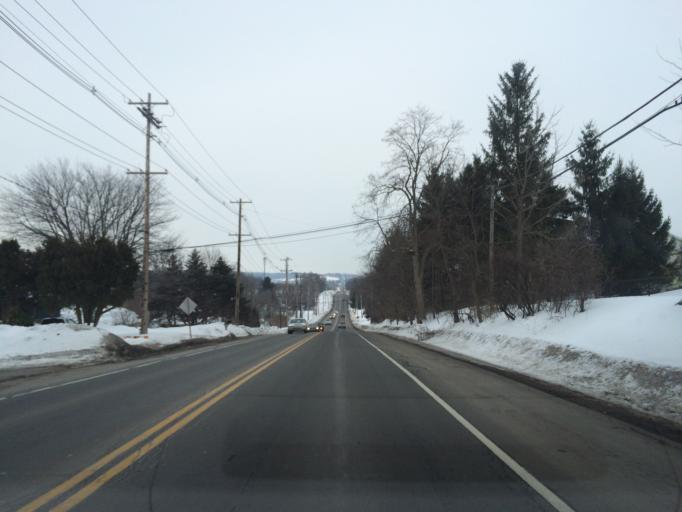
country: US
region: New York
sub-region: Monroe County
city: Fairport
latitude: 43.0893
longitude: -77.4321
